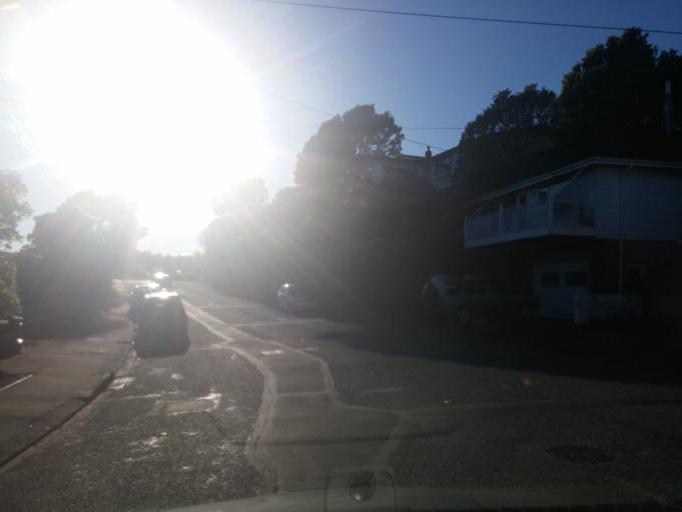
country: NZ
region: Wellington
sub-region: Wellington City
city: Kelburn
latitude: -41.2683
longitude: 174.7643
